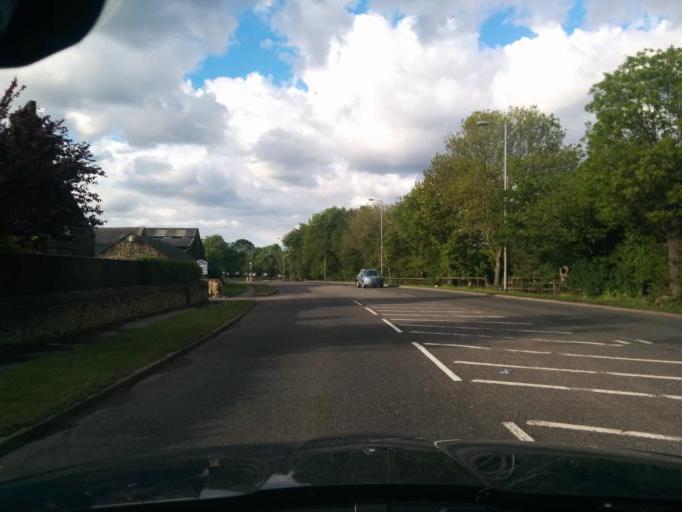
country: GB
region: England
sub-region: Northumberland
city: Bedlington
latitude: 55.1251
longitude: -1.6010
